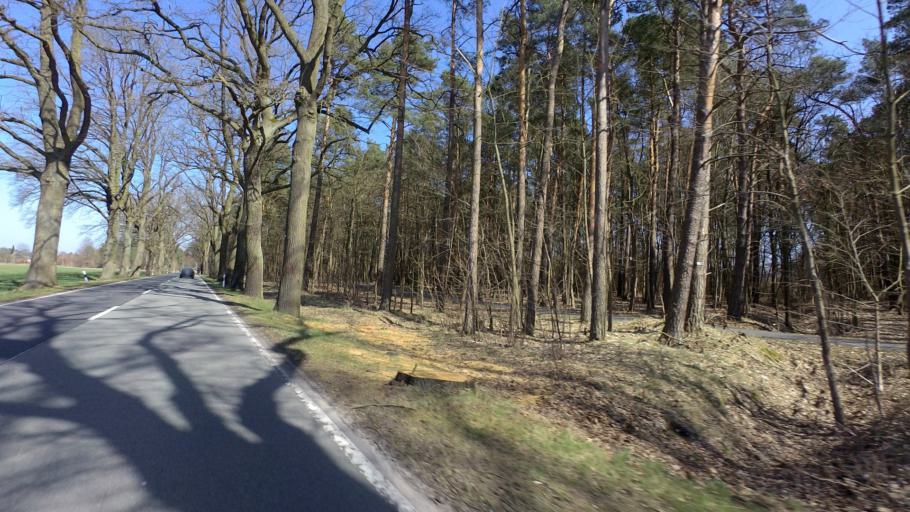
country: DE
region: Brandenburg
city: Lindow
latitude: 52.9530
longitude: 12.9785
